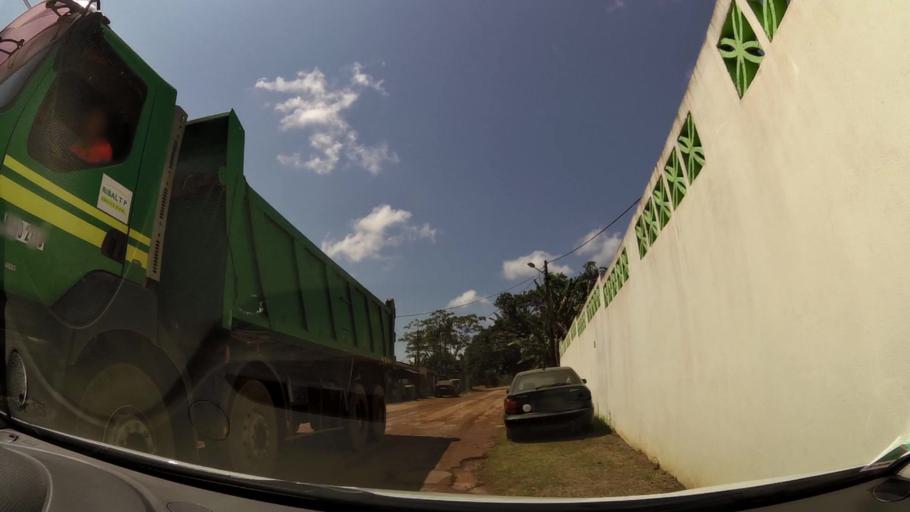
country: GF
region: Guyane
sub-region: Guyane
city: Cayenne
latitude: 4.9142
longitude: -52.3180
